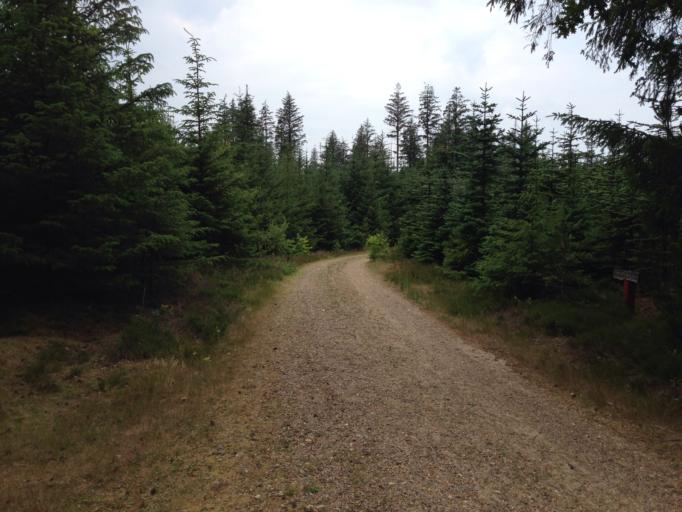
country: DK
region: South Denmark
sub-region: Varde Kommune
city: Oksbol
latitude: 55.7506
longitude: 8.2383
